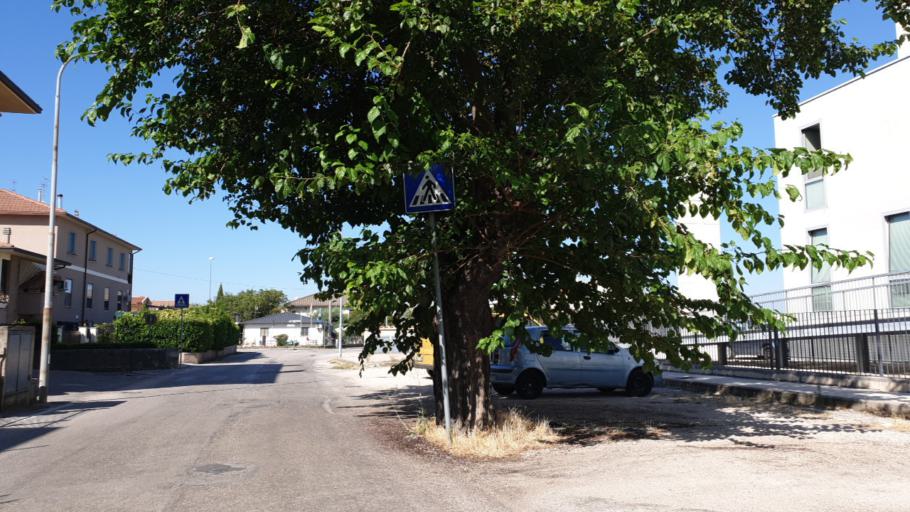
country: IT
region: Umbria
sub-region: Provincia di Perugia
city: Foligno
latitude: 42.9560
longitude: 12.6890
